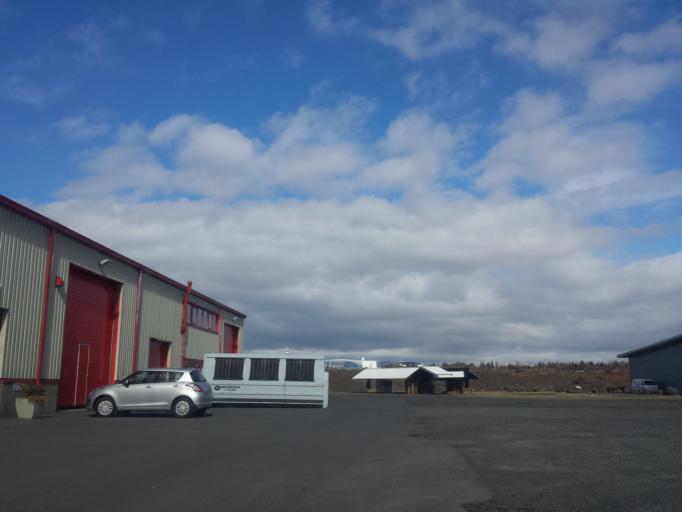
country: IS
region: Capital Region
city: Gardabaer
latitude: 64.0813
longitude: -21.9292
